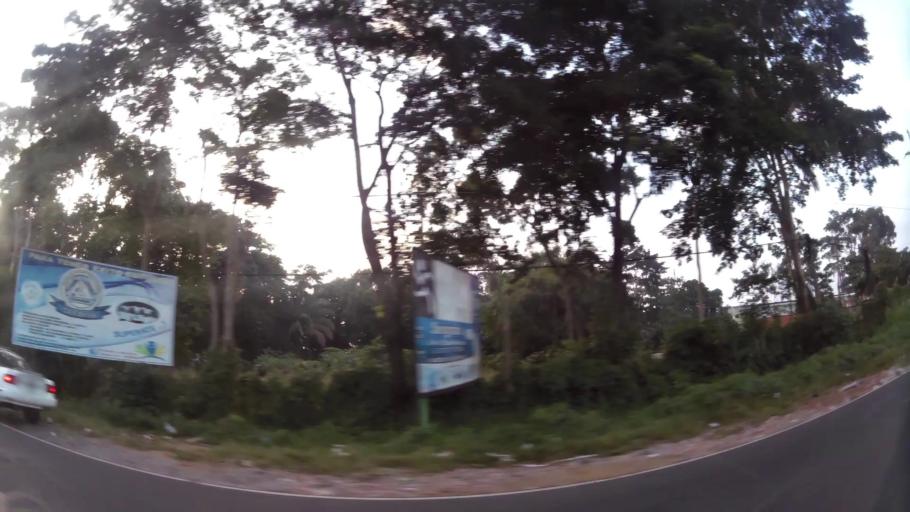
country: GT
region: Retalhuleu
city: San Sebastian
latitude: 14.5715
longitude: -91.6486
